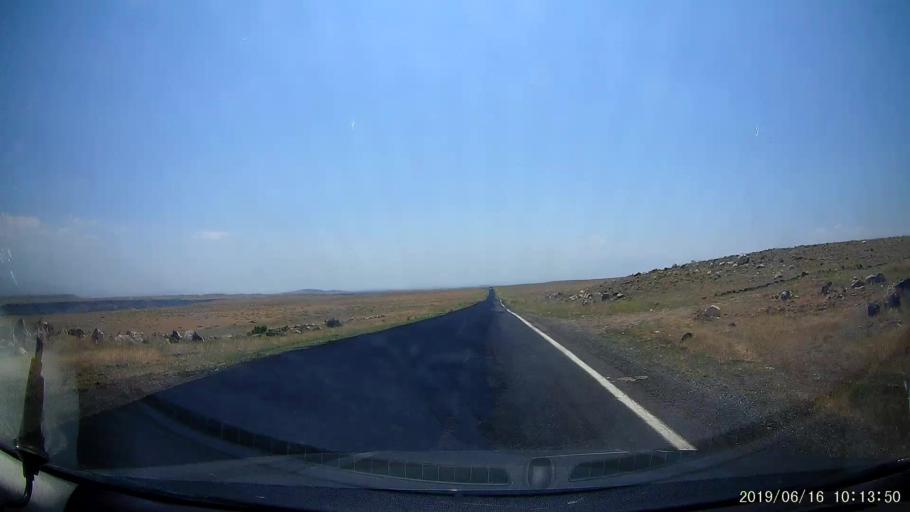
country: TR
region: Igdir
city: Tuzluca
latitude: 40.1901
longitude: 43.6501
